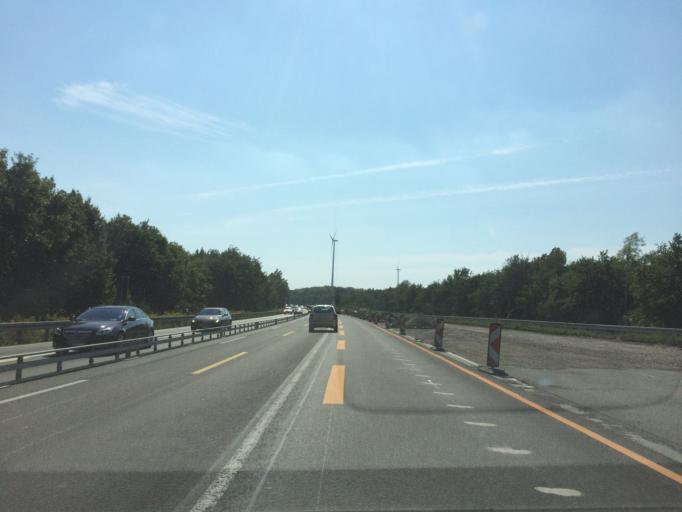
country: DE
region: North Rhine-Westphalia
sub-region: Regierungsbezirk Munster
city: Haltern
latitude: 51.6989
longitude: 7.1472
